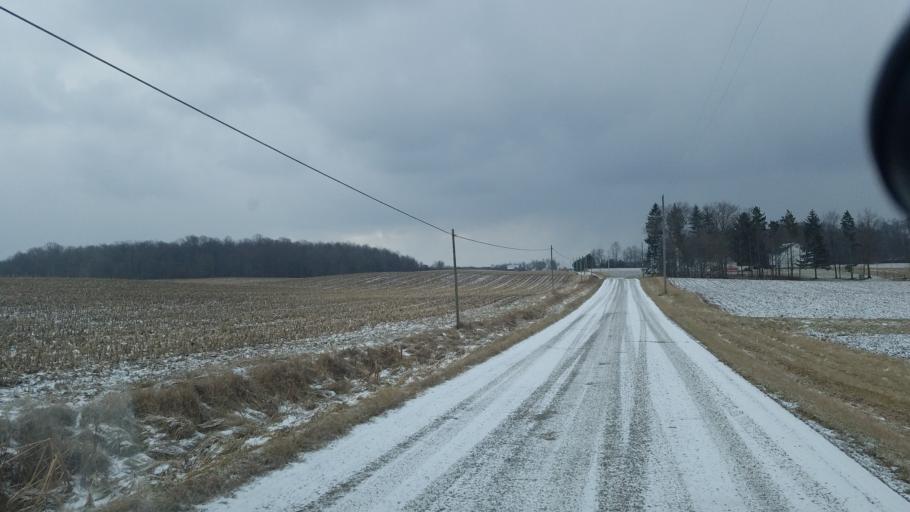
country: US
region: Ohio
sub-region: Morrow County
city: Mount Gilead
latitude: 40.5975
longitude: -82.7904
